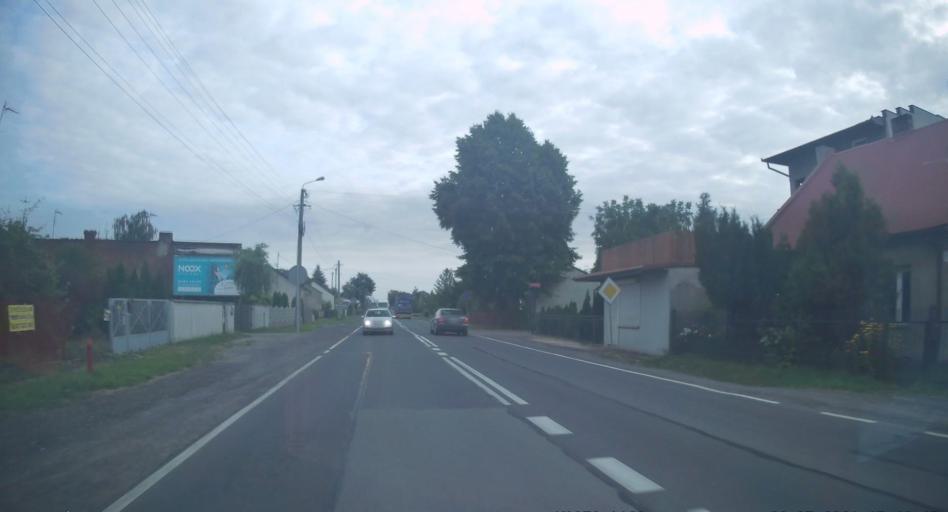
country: PL
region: Lodz Voivodeship
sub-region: Powiat radomszczanski
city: Radomsko
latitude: 51.0941
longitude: 19.4585
